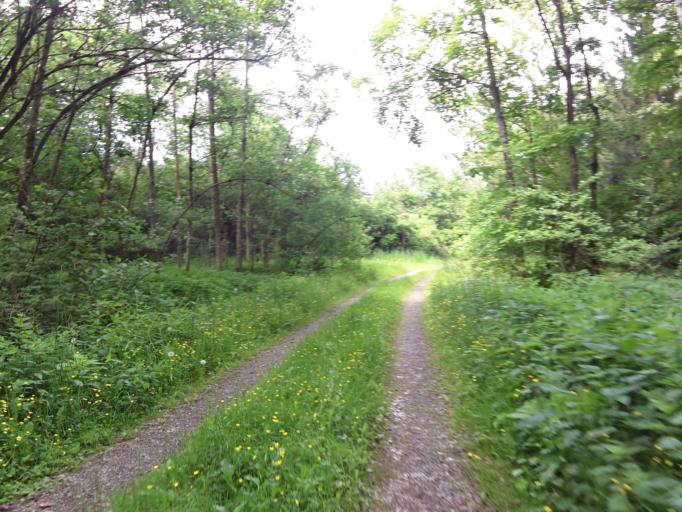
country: DE
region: Bavaria
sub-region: Regierungsbezirk Unterfranken
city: Kleinrinderfeld
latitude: 49.7099
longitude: 9.8085
